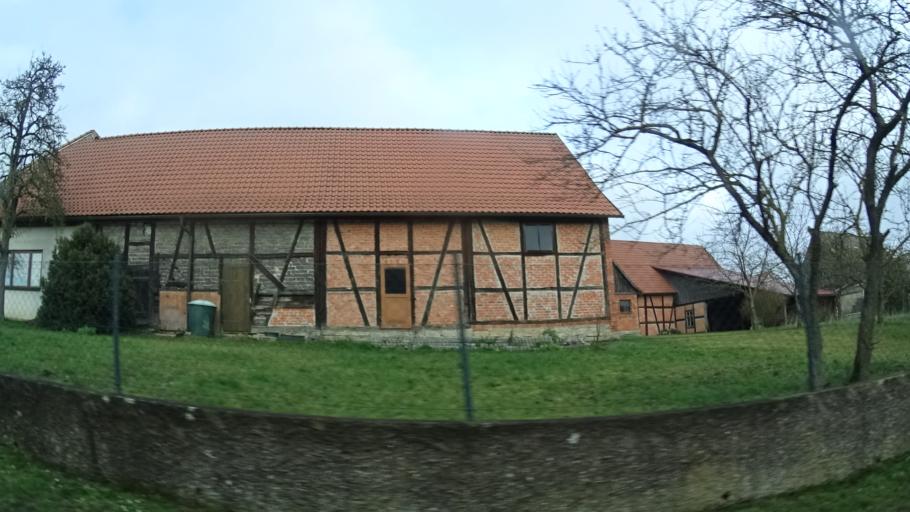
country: DE
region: Thuringia
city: Kuhndorf
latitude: 50.6076
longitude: 10.4892
